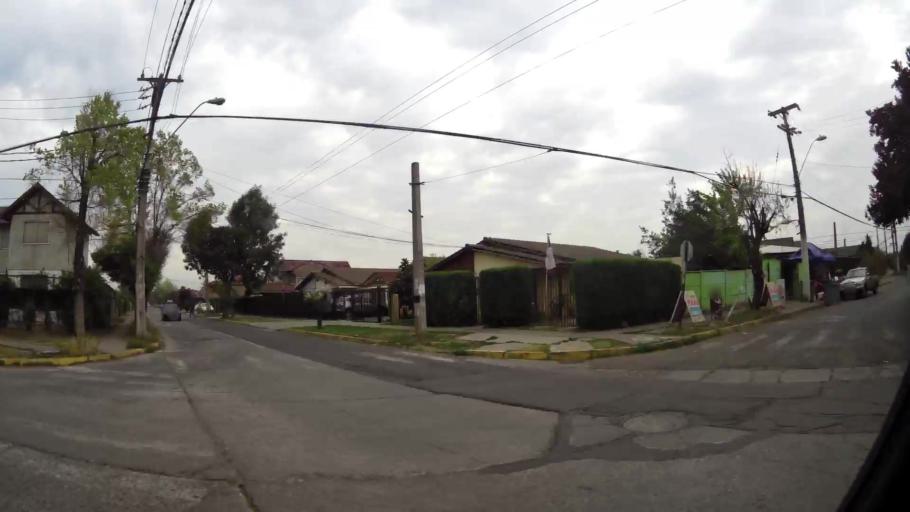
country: CL
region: Santiago Metropolitan
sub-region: Provincia de Santiago
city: Lo Prado
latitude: -33.4951
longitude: -70.7511
